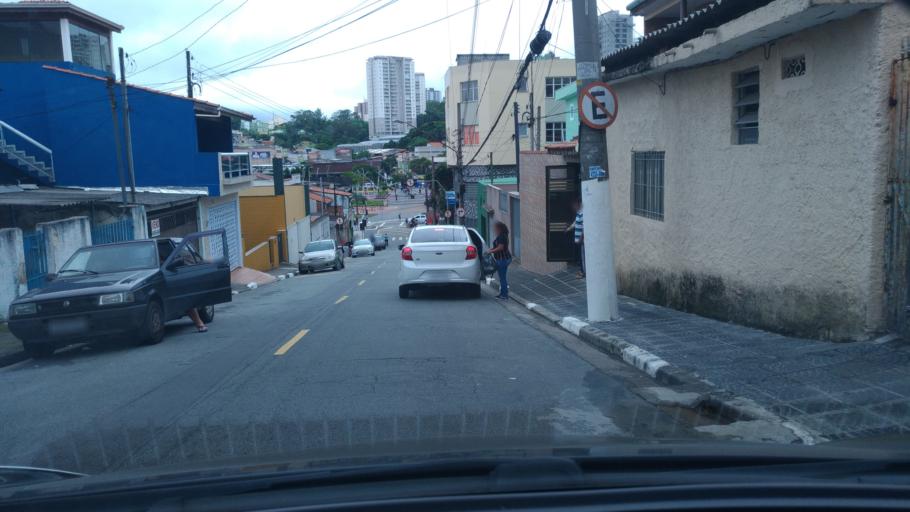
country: BR
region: Sao Paulo
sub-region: Diadema
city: Diadema
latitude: -23.6843
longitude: -46.6215
